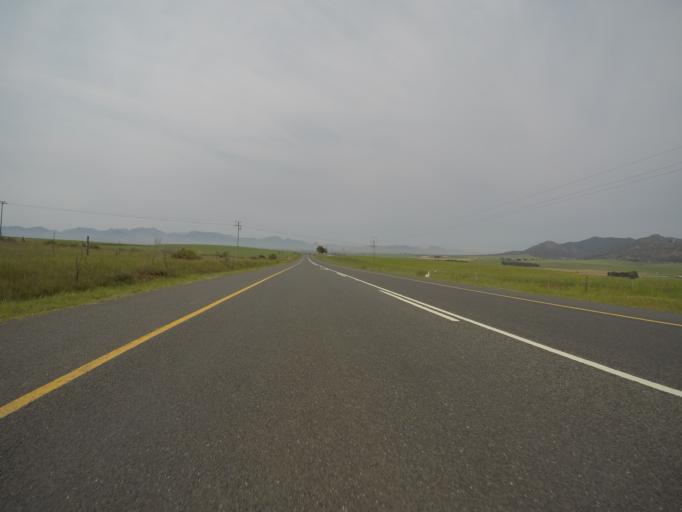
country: ZA
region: Western Cape
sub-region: West Coast District Municipality
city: Malmesbury
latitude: -33.5322
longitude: 18.8519
